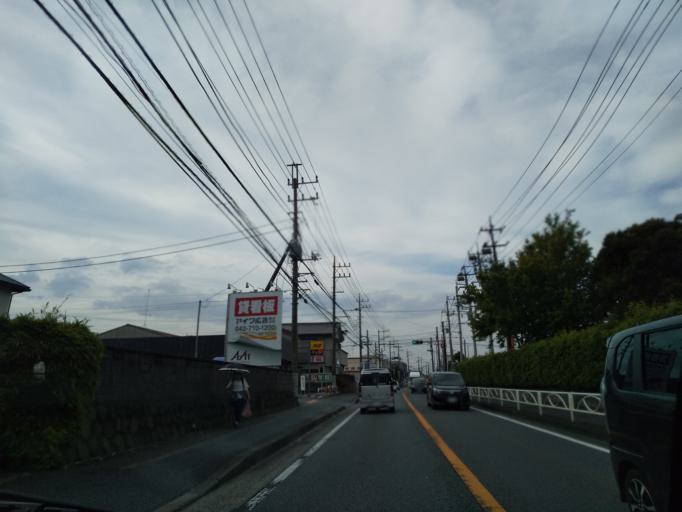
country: JP
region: Kanagawa
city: Zama
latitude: 35.4871
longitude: 139.3405
